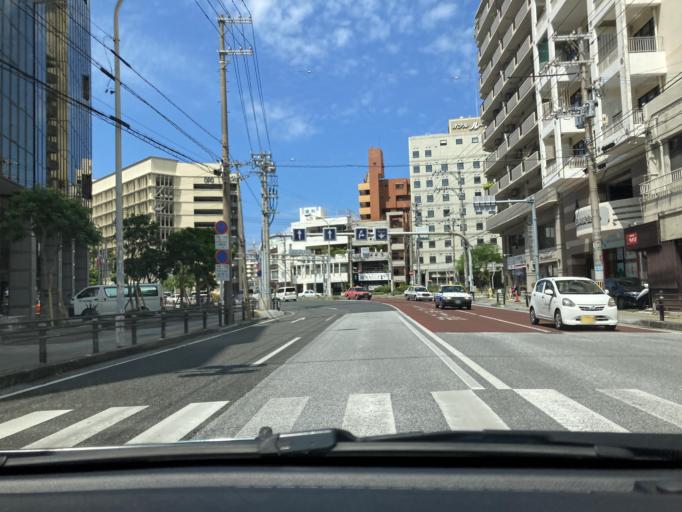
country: JP
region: Okinawa
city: Naha-shi
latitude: 26.2095
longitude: 127.6785
